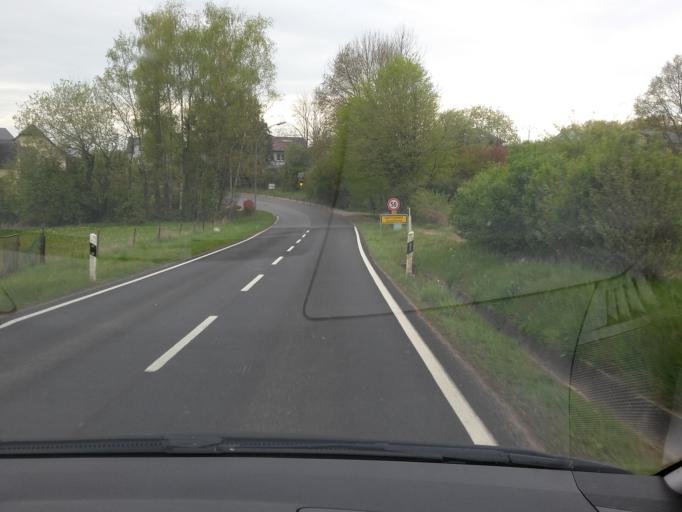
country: LU
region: Luxembourg
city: Hautcharage
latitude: 49.5825
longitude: 5.9092
